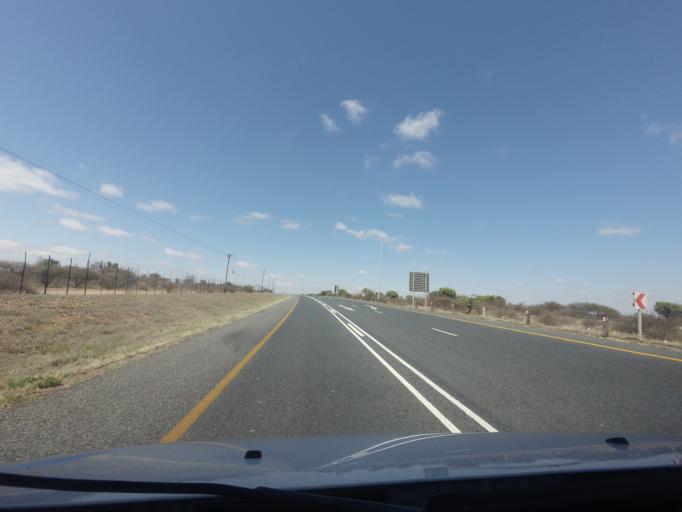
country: ZA
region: Limpopo
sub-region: Vhembe District Municipality
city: Louis Trichardt
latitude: -23.3735
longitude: 29.7698
